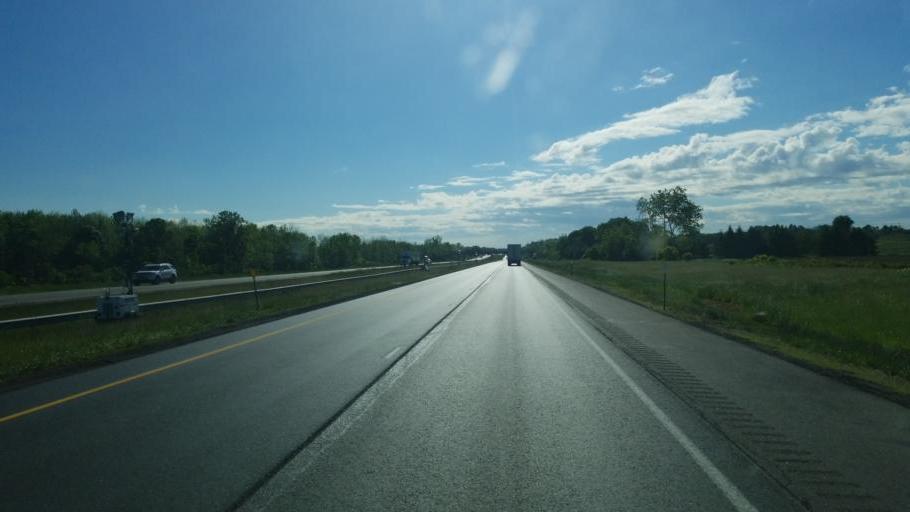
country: US
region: New York
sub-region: Livingston County
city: Caledonia
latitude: 43.0299
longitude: -77.8840
